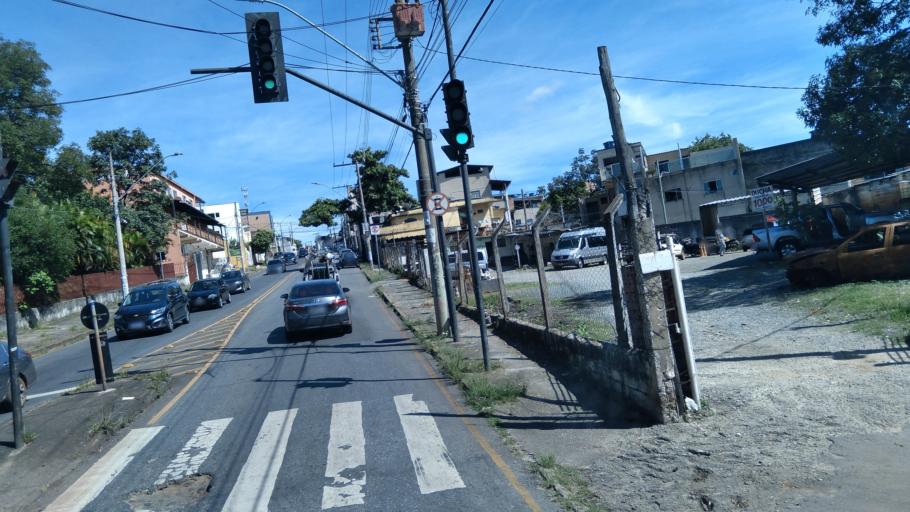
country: BR
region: Minas Gerais
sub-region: Contagem
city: Contagem
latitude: -19.8912
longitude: -44.0104
